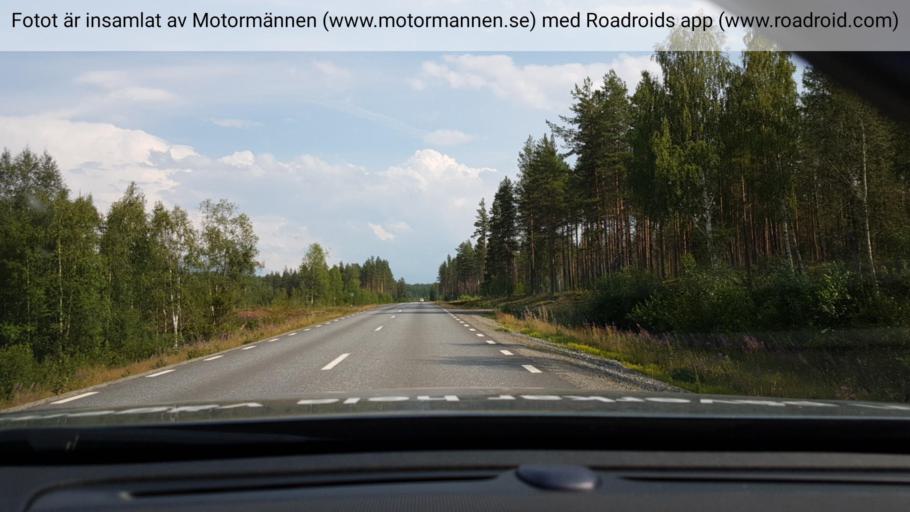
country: SE
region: Vaesterbotten
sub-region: Bjurholms Kommun
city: Bjurholm
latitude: 64.3847
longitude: 19.1133
